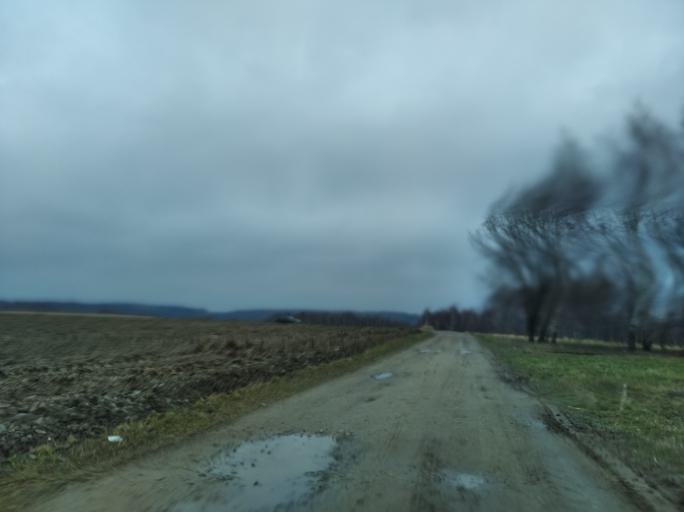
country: PL
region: Subcarpathian Voivodeship
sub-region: Powiat strzyzowski
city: Strzyzow
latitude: 49.8845
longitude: 21.8016
